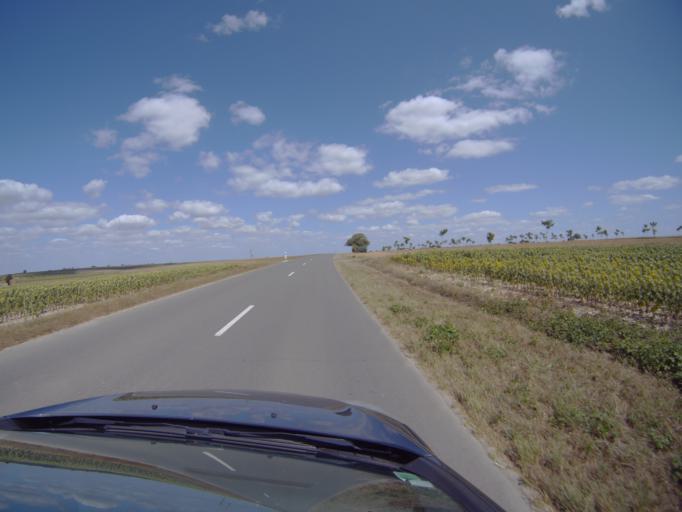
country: FR
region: Poitou-Charentes
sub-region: Departement des Deux-Sevres
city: Saint-Hilaire-la-Palud
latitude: 46.2635
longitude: -0.6898
